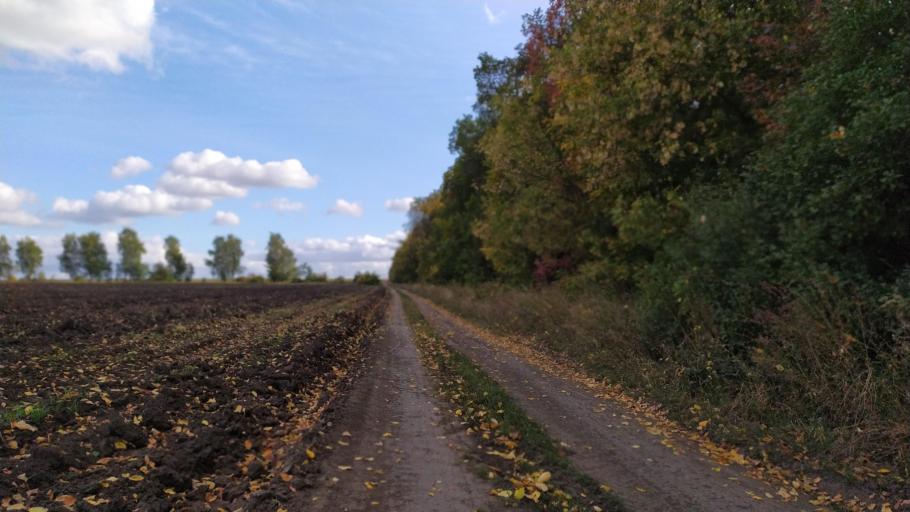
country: RU
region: Kursk
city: Kursk
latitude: 51.6240
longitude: 36.1610
